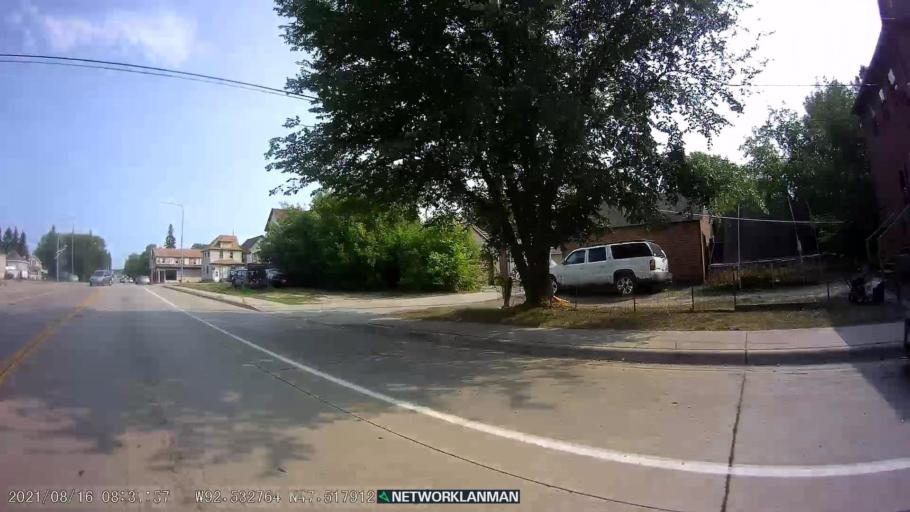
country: US
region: Minnesota
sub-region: Saint Louis County
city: Virginia
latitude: 47.5181
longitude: -92.5328
